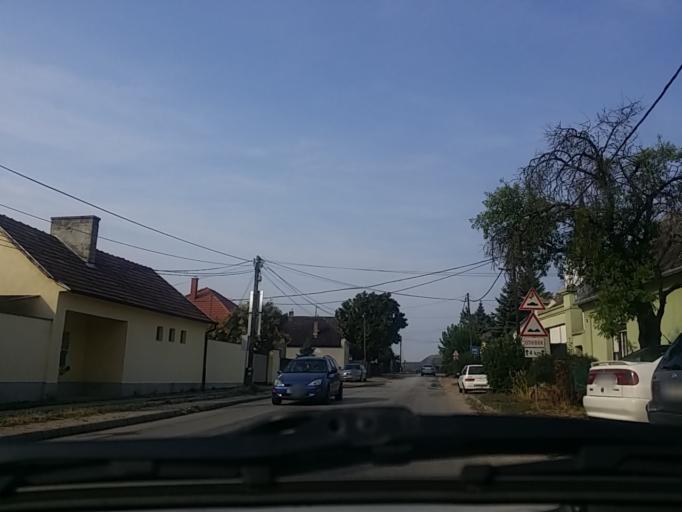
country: HU
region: Fejer
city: Csakvar
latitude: 47.3933
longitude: 18.4605
